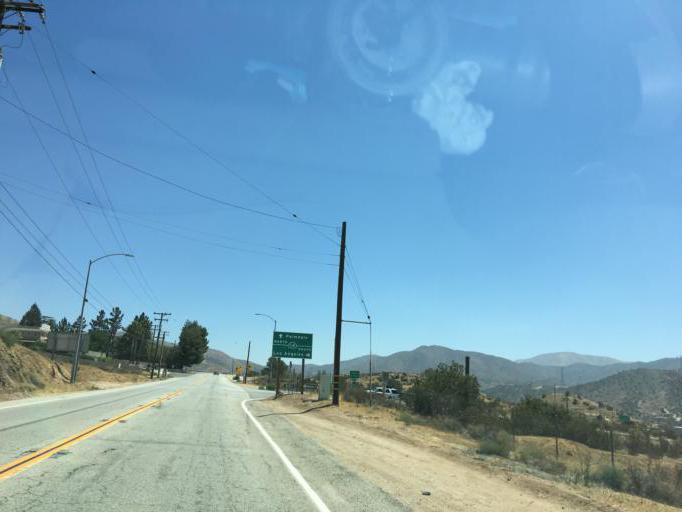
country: US
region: California
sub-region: Los Angeles County
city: Vincent
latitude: 34.4871
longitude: -118.1448
